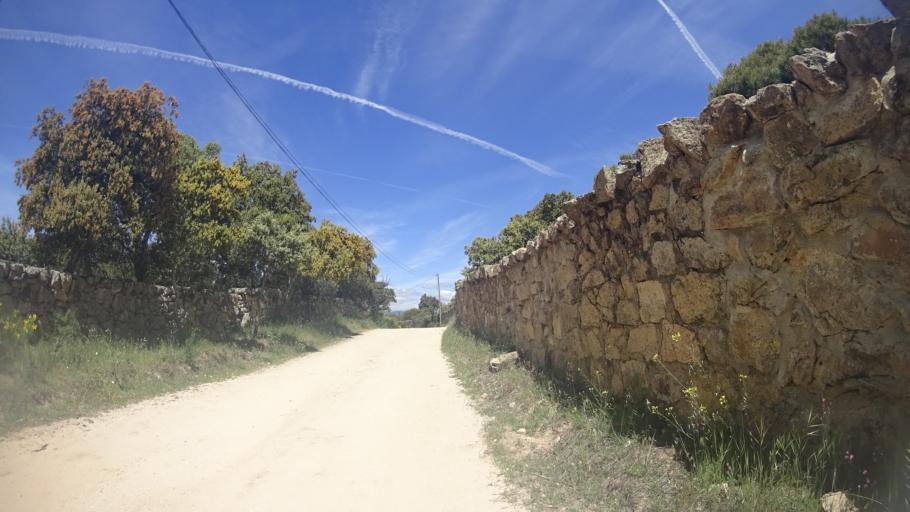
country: ES
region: Madrid
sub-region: Provincia de Madrid
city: Galapagar
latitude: 40.5587
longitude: -3.9854
